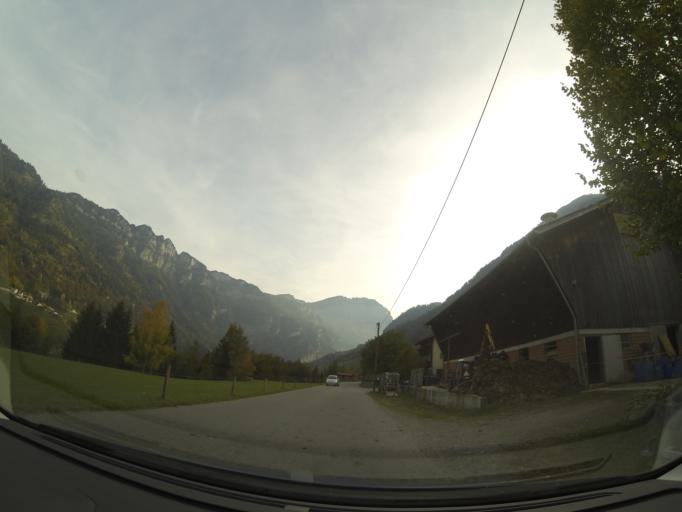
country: CH
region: Saint Gallen
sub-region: Wahlkreis Sarganserland
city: Bad Ragaz
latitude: 46.9622
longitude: 9.4751
